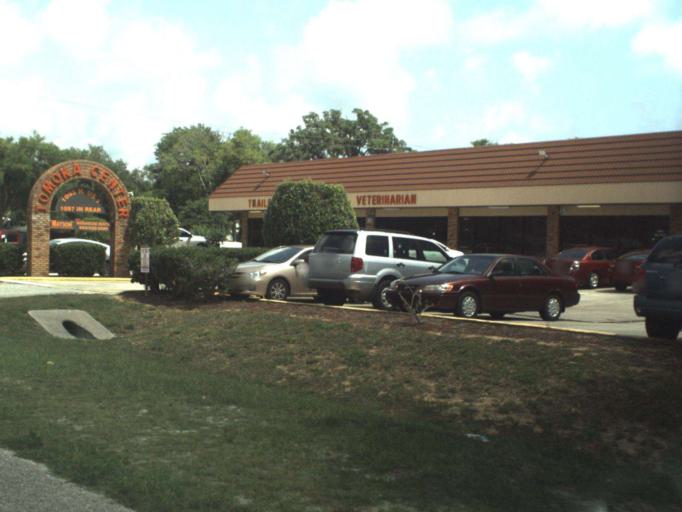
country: US
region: Florida
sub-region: Volusia County
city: Ormond-by-the-Sea
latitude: 29.3121
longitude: -81.1014
